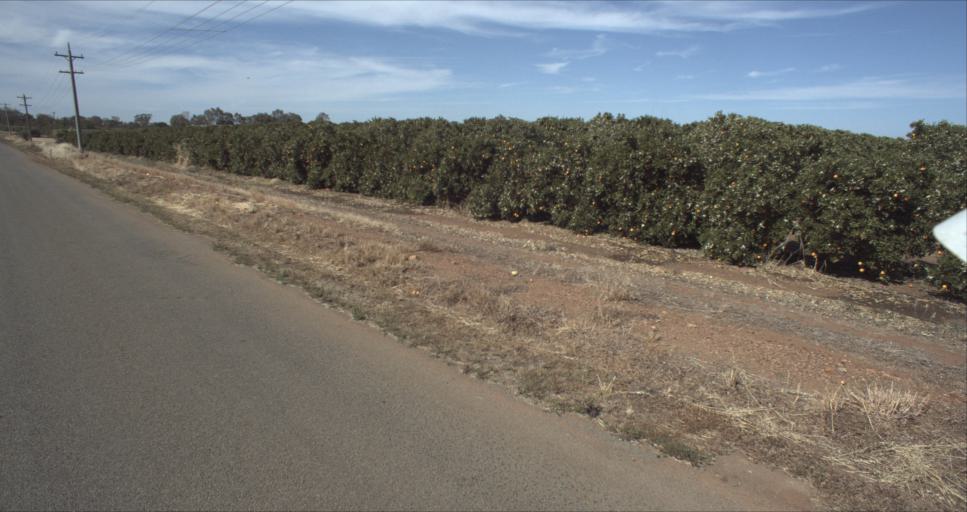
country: AU
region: New South Wales
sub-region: Leeton
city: Leeton
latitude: -34.5748
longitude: 146.4764
